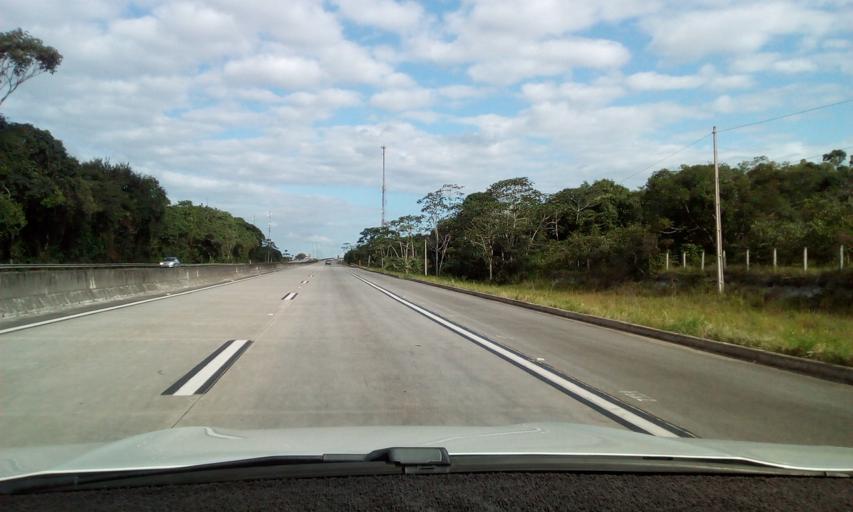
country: BR
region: Paraiba
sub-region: Mamanguape
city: Mamanguape
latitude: -6.9816
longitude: -35.0758
